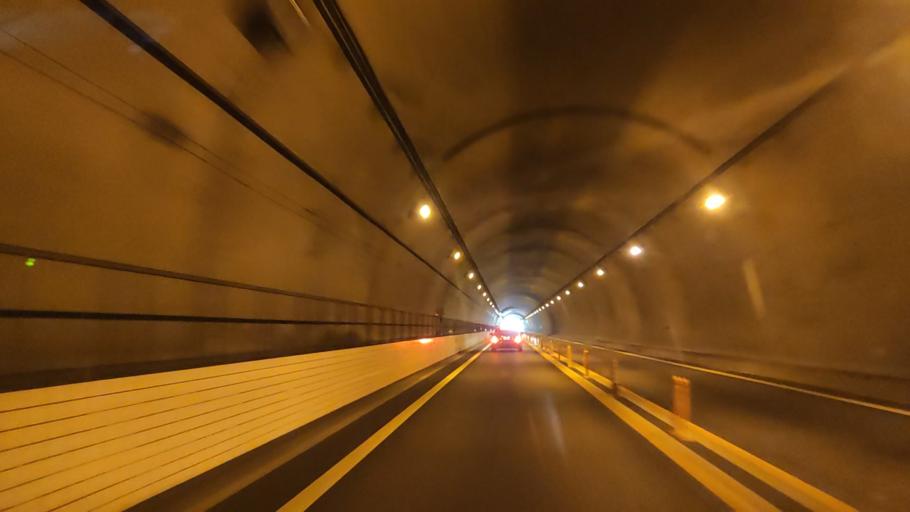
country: JP
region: Tokushima
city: Ikedacho
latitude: 34.0230
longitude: 133.7946
